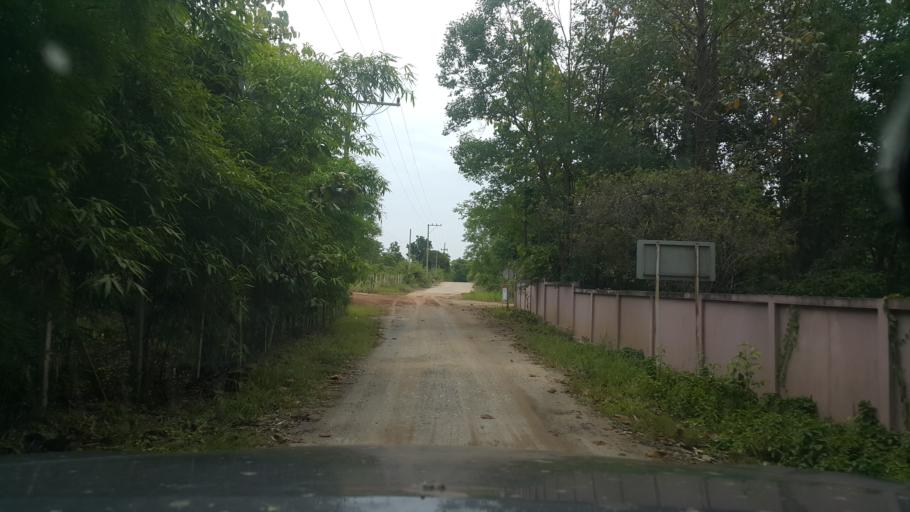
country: TH
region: Chiang Mai
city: San Pa Tong
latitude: 18.6510
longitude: 98.8515
